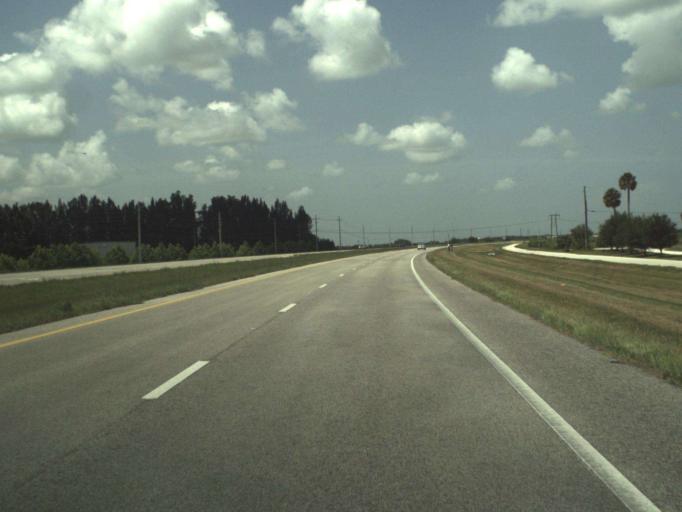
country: US
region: Florida
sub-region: Saint Lucie County
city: Fort Pierce South
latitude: 27.3923
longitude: -80.4599
